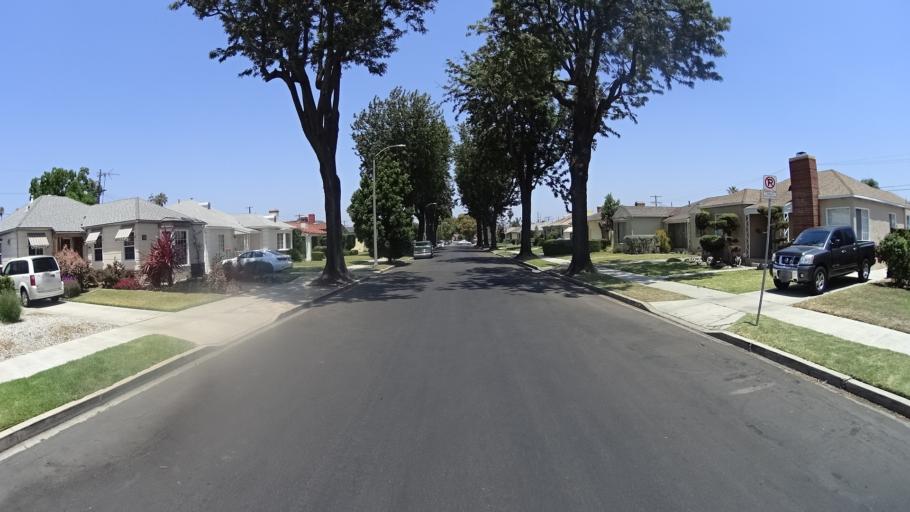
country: US
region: California
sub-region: Los Angeles County
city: View Park-Windsor Hills
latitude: 34.0171
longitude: -118.3281
